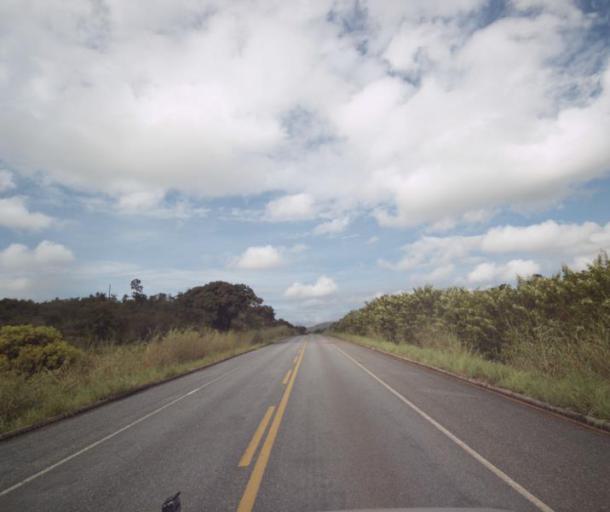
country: BR
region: Goias
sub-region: Pirenopolis
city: Pirenopolis
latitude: -15.6161
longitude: -48.6606
